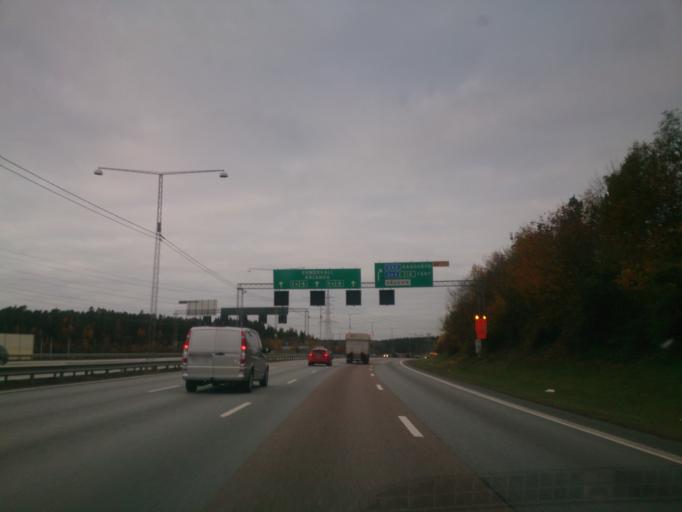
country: SE
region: Stockholm
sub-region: Sollentuna Kommun
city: Sollentuna
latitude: 59.4281
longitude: 17.9217
